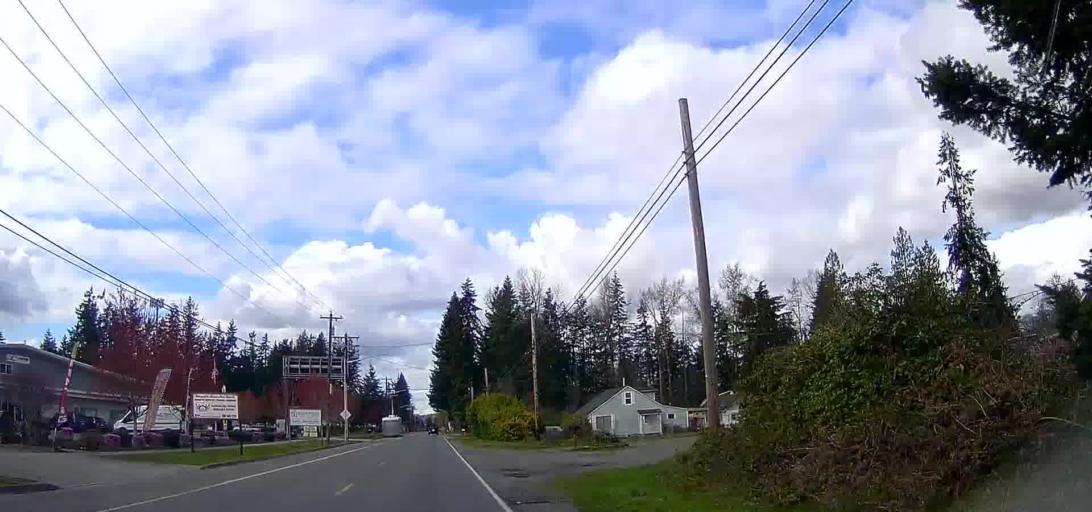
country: US
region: Washington
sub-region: Snohomish County
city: Smokey Point
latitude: 48.1678
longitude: -122.1862
